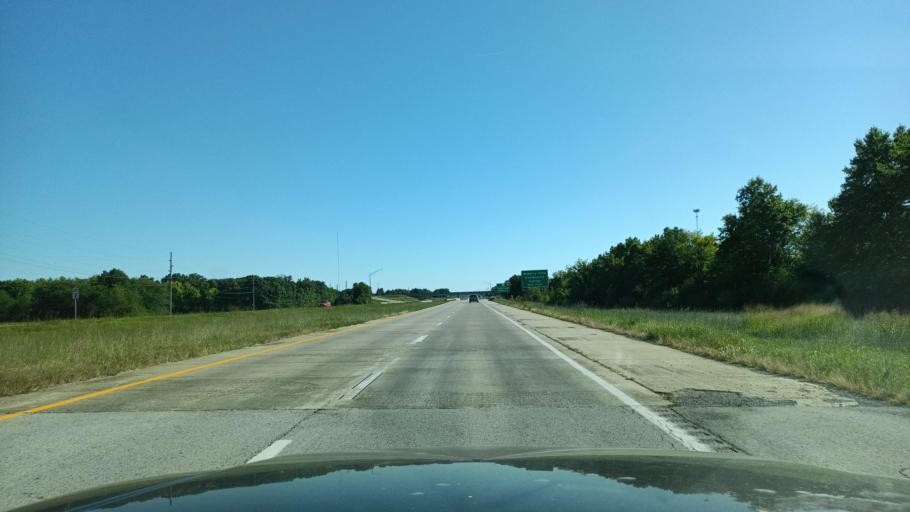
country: US
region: Missouri
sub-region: Randolph County
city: Moberly
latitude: 39.4234
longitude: -92.4120
